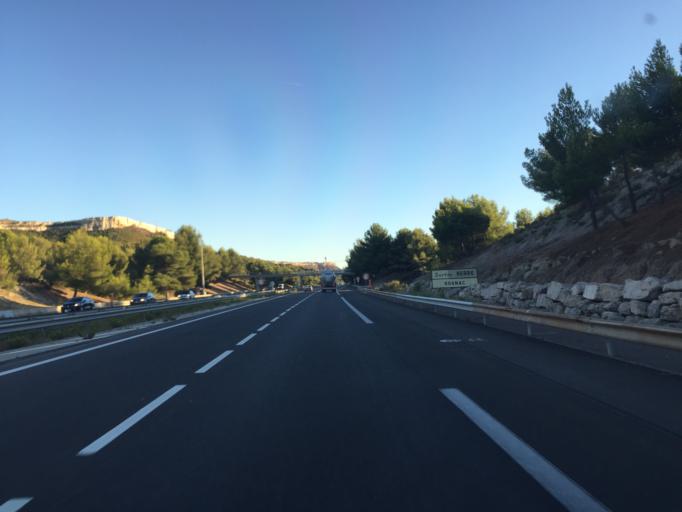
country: FR
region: Provence-Alpes-Cote d'Azur
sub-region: Departement des Bouches-du-Rhone
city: Rognac
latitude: 43.5004
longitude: 5.2383
